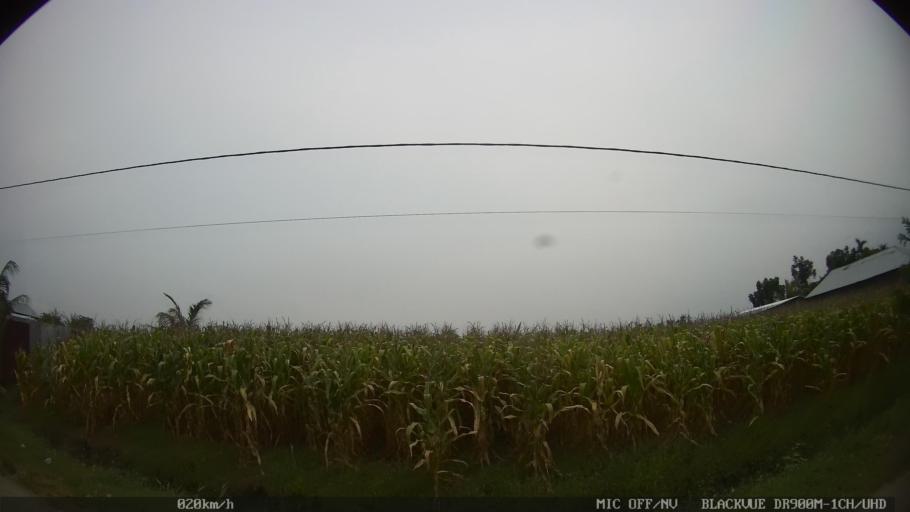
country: ID
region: North Sumatra
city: Medan
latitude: 3.5735
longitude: 98.7361
